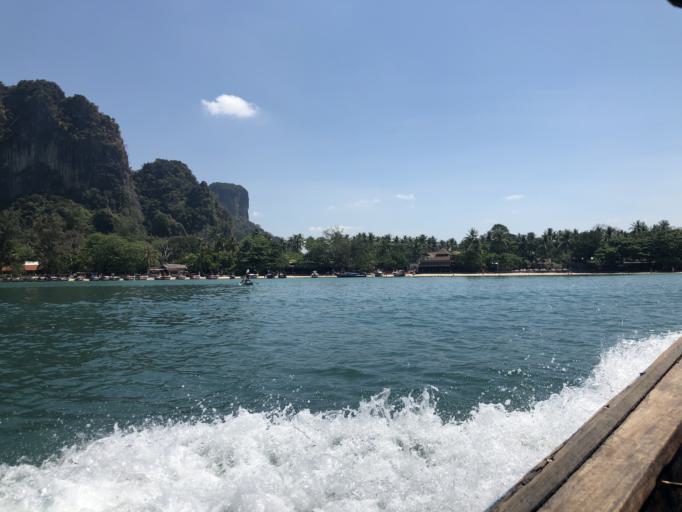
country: TH
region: Phangnga
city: Ban Ao Nang
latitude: 8.0104
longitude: 98.8362
